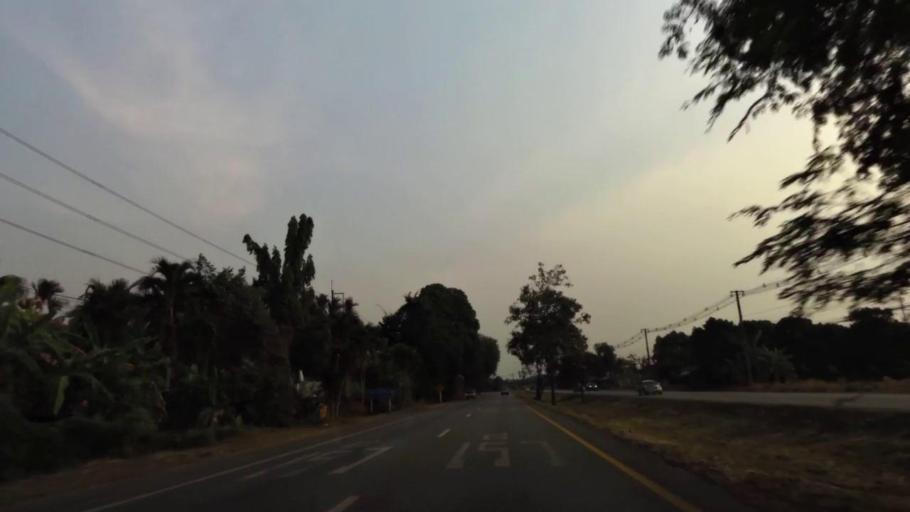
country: TH
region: Chanthaburi
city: Khlung
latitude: 12.4904
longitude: 102.1741
